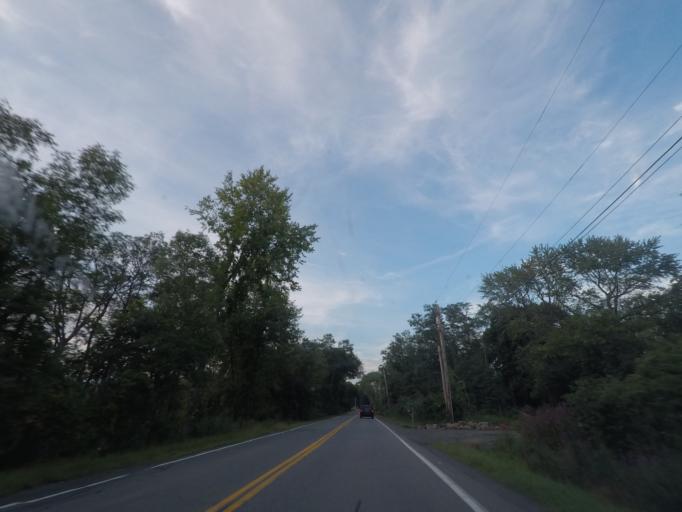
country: US
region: New York
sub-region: Schenectady County
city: Niskayuna
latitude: 42.7757
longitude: -73.7942
